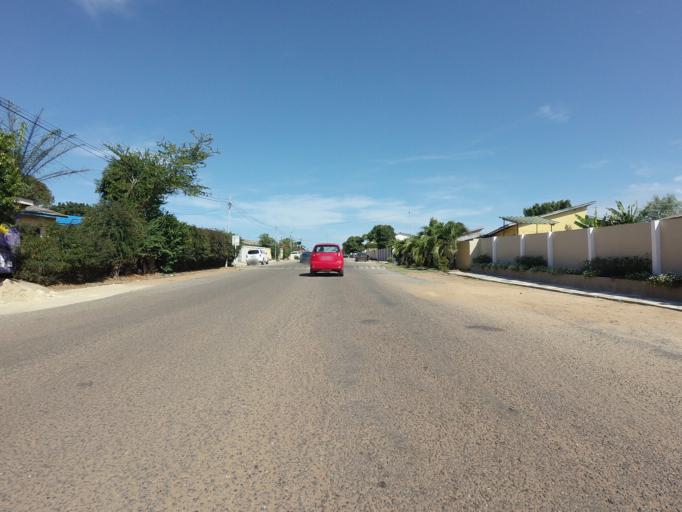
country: GH
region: Greater Accra
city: Accra
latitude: 5.5633
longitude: -0.1711
